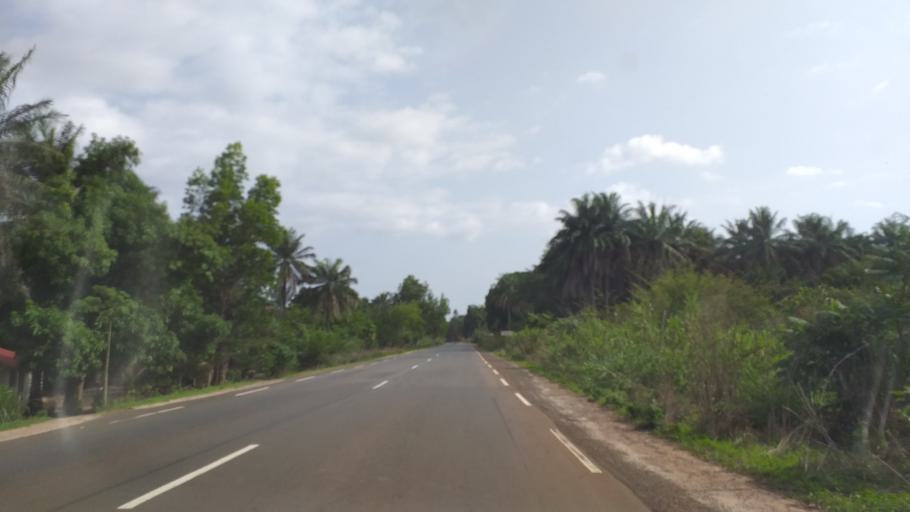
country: GN
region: Boke
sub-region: Boke Prefecture
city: Sangueya
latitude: 10.5693
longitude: -14.3984
